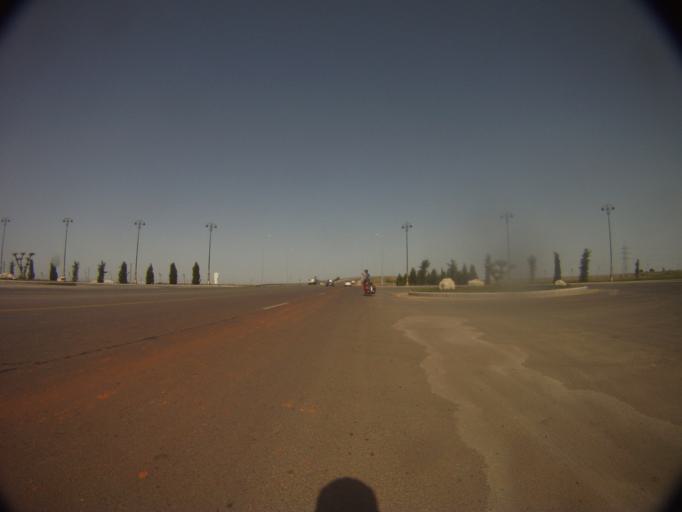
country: AZ
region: Samux
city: Samux
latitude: 40.6894
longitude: 46.4903
